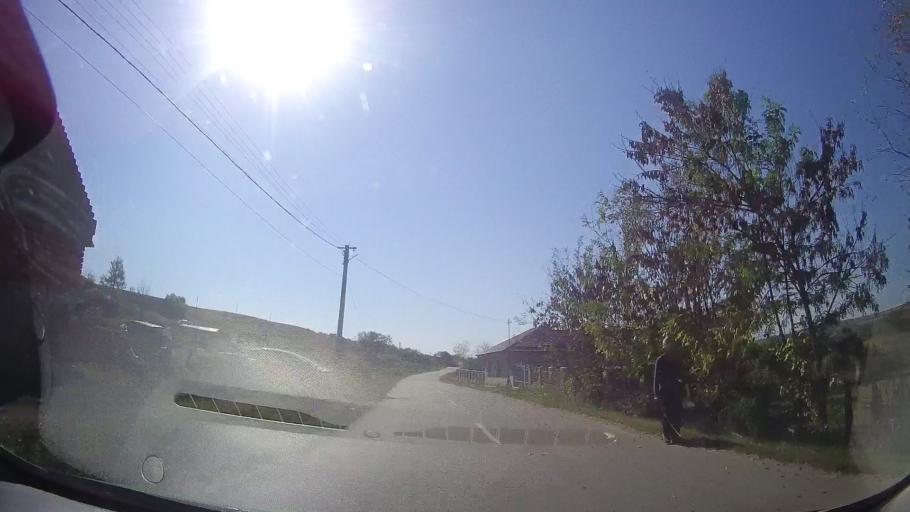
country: RO
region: Timis
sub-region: Comuna Bethausen
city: Bethausen
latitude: 45.8577
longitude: 21.9679
